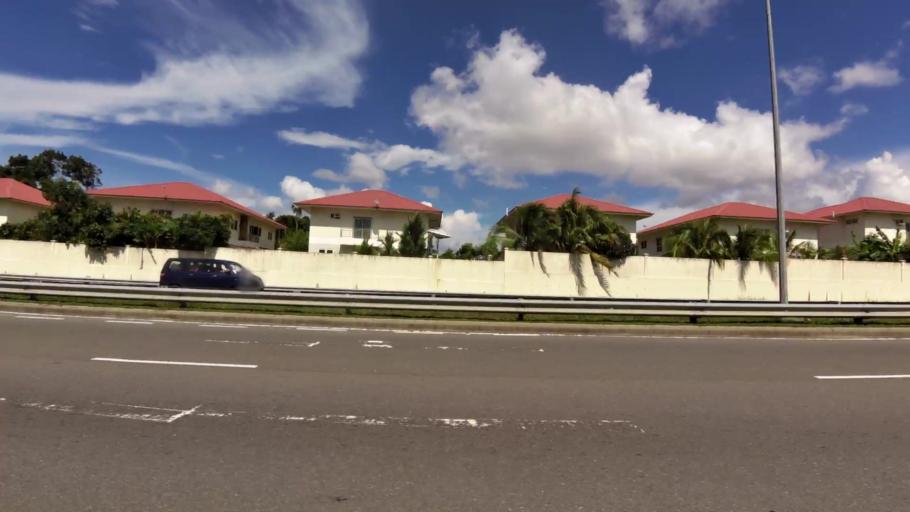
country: BN
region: Brunei and Muara
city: Bandar Seri Begawan
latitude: 4.9729
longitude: 114.9541
